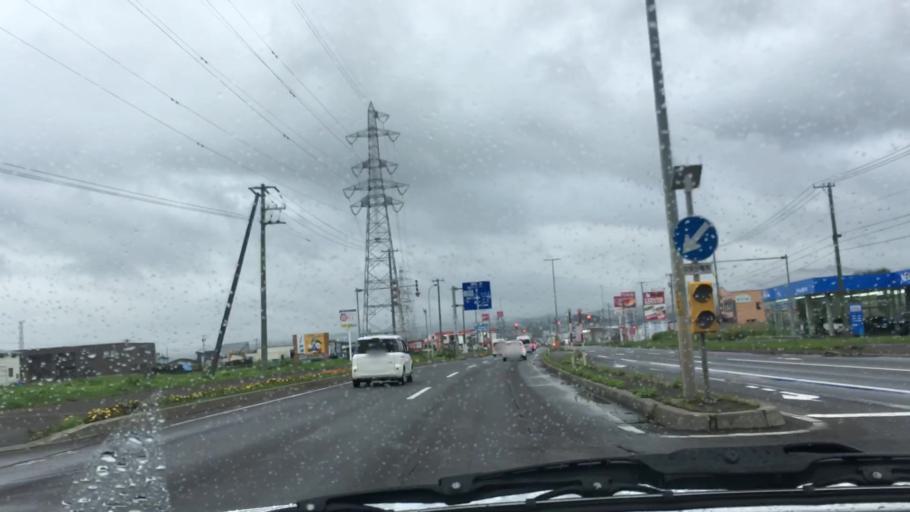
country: JP
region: Hokkaido
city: Nanae
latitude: 42.2537
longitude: 140.2835
